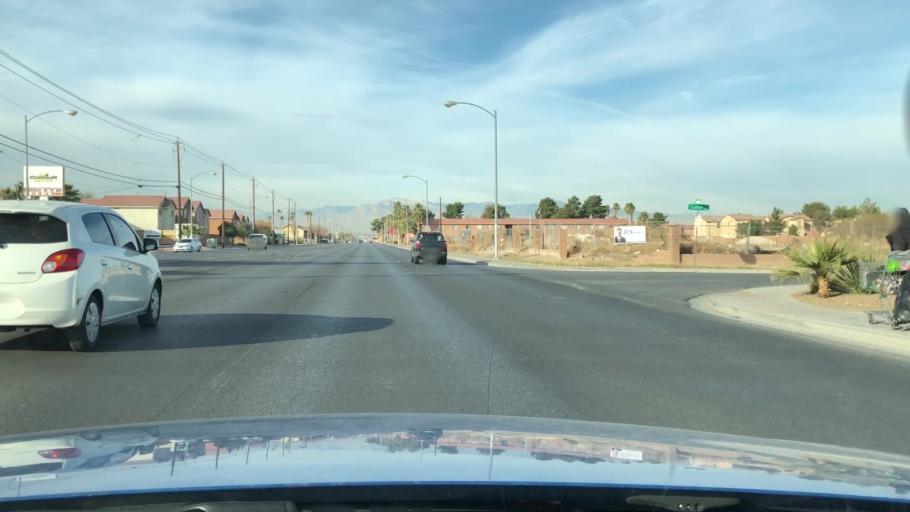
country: US
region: Nevada
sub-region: Clark County
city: Sunrise Manor
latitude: 36.1958
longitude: -115.0912
